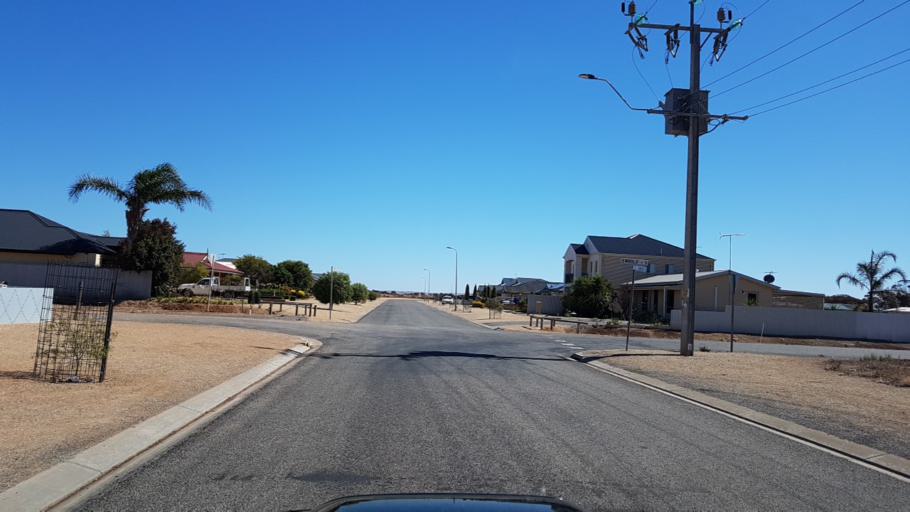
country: AU
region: South Australia
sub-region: Wakefield
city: Balaklava
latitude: -34.1808
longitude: 138.1519
